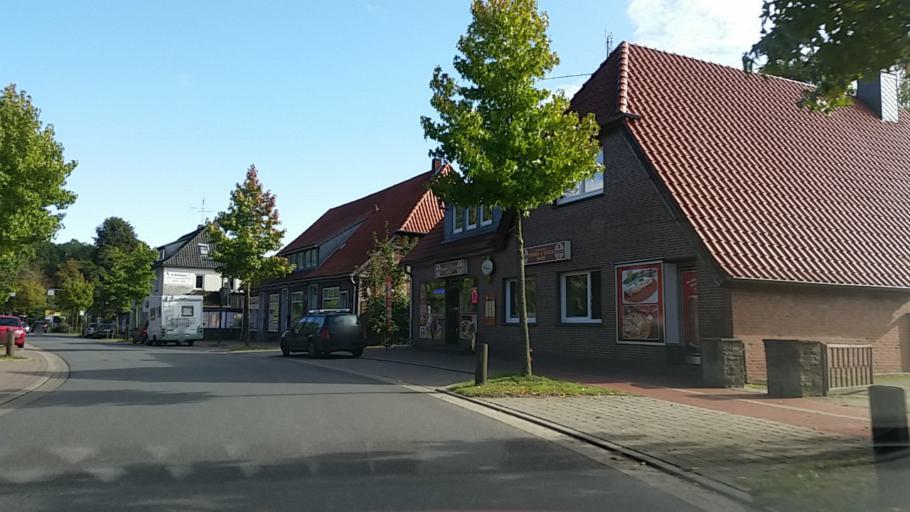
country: DE
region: Lower Saxony
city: Neuenkirchen
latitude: 53.0327
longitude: 9.7053
